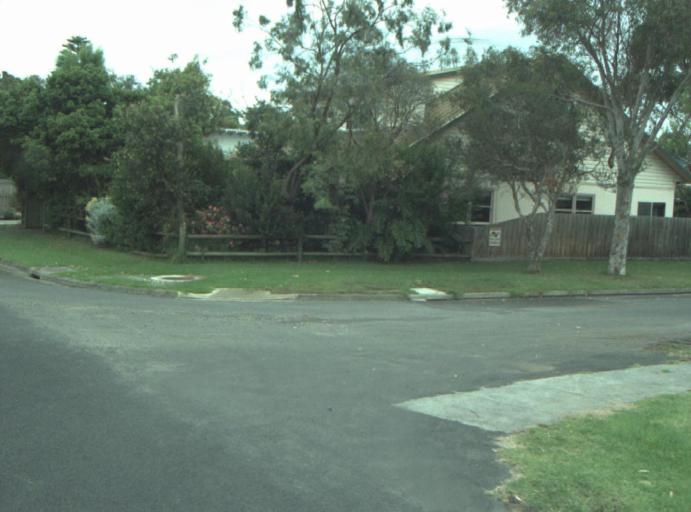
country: AU
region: Victoria
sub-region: Greater Geelong
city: East Geelong
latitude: -38.1547
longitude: 144.3840
